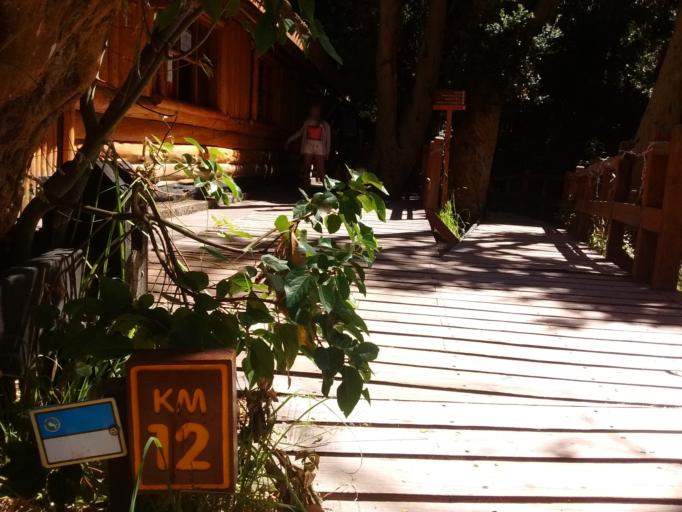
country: AR
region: Neuquen
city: Villa La Angostura
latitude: -40.8580
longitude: -71.6153
